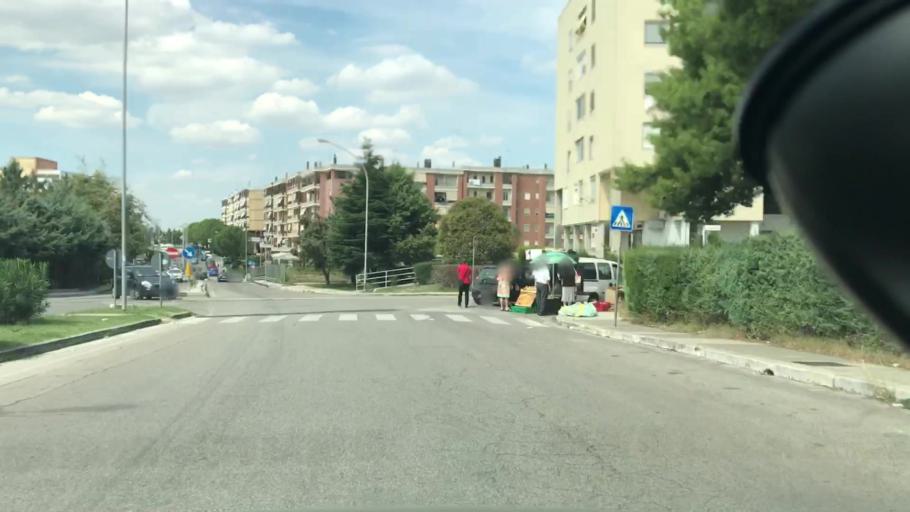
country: IT
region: Basilicate
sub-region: Provincia di Matera
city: Matera
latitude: 40.6765
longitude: 16.5832
